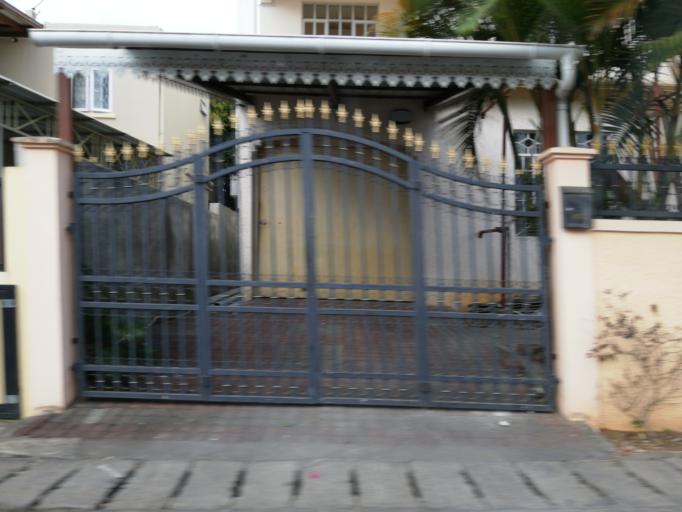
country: MU
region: Black River
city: Petite Riviere
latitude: -20.2183
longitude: 57.4606
